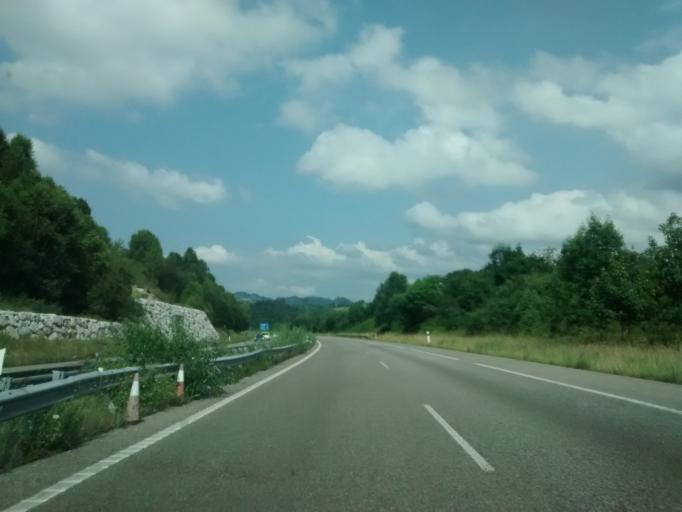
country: ES
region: Asturias
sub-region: Province of Asturias
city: Sama
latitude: 43.3452
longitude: -5.6894
